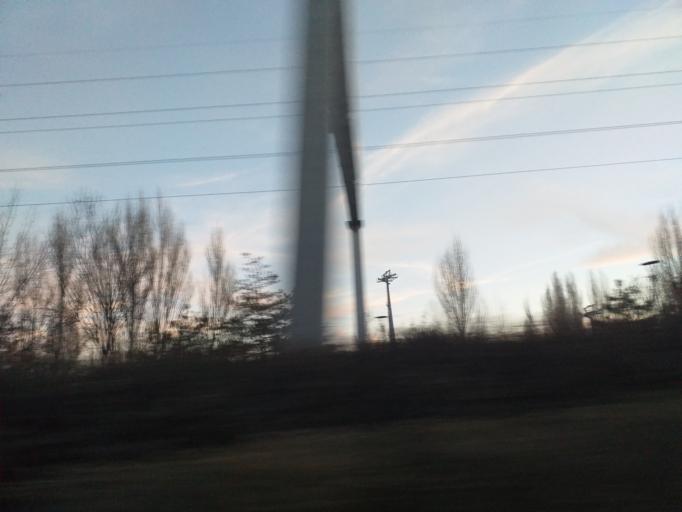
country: TR
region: Ankara
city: Ankara
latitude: 39.9539
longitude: 32.8138
